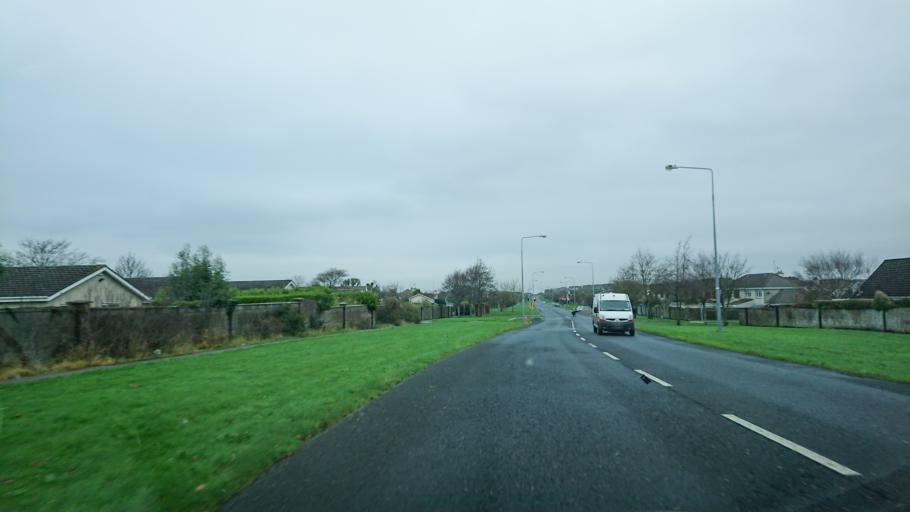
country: IE
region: Munster
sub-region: Waterford
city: Tra Mhor
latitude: 52.1596
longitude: -7.1688
